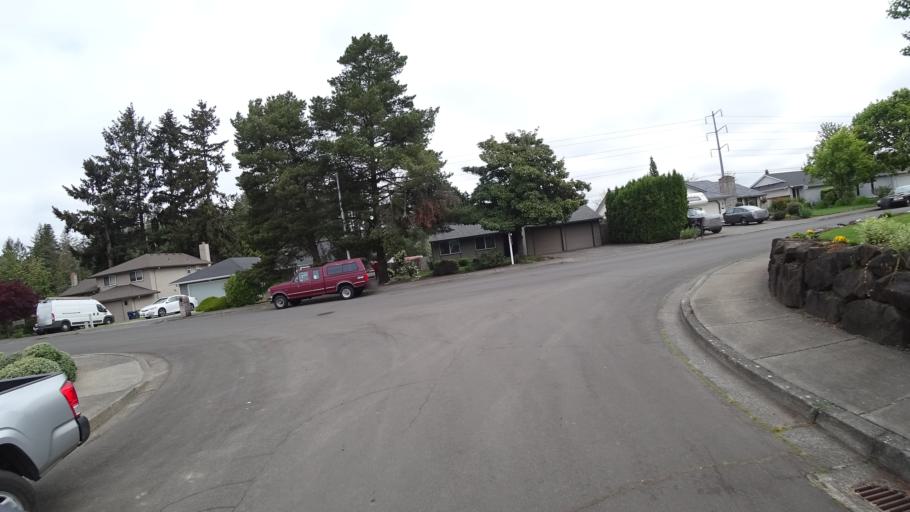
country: US
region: Oregon
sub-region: Washington County
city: Aloha
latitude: 45.5175
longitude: -122.8730
